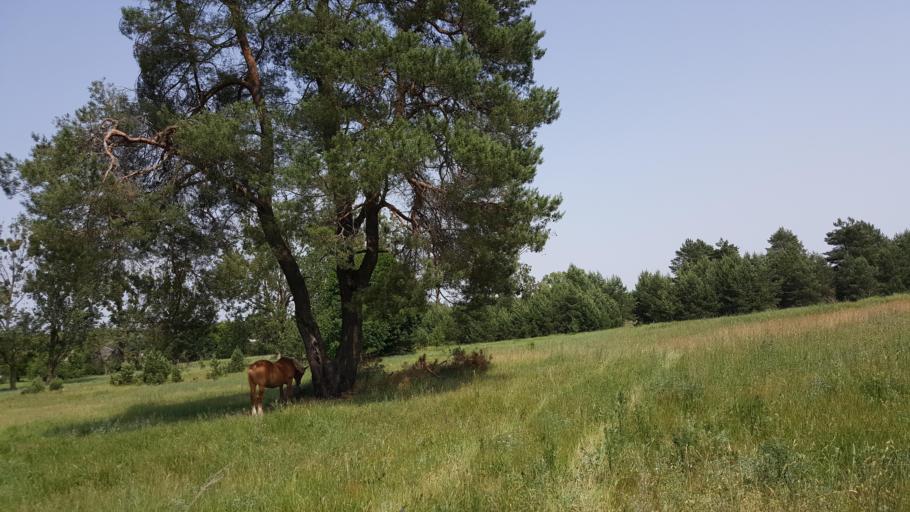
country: BY
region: Brest
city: Kamyanyuki
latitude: 52.5201
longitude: 23.8468
